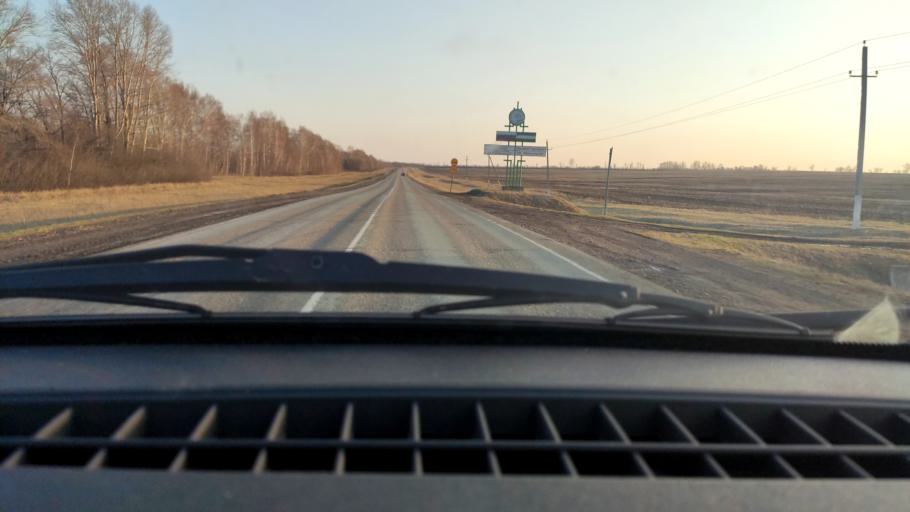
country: RU
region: Bashkortostan
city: Davlekanovo
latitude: 54.3414
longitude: 55.1728
